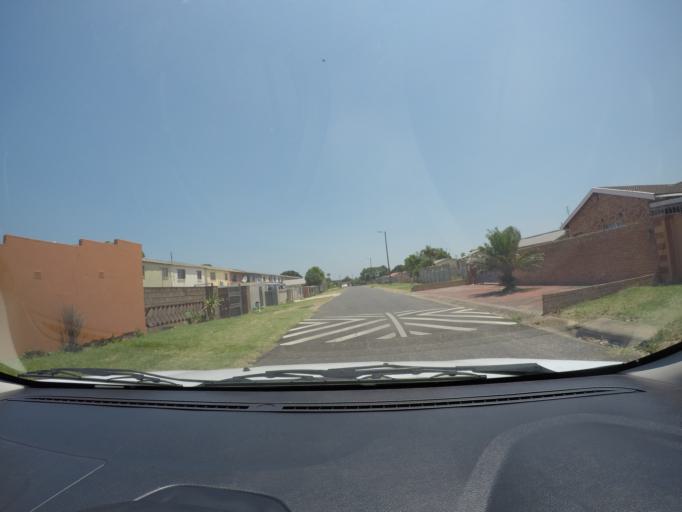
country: ZA
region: KwaZulu-Natal
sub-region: uThungulu District Municipality
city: eSikhawini
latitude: -28.8844
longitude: 31.8912
